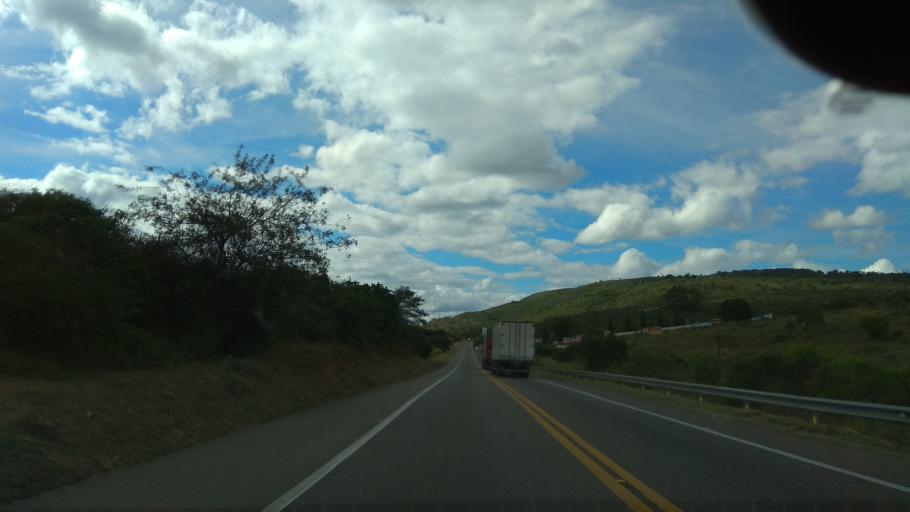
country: BR
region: Bahia
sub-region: Amargosa
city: Amargosa
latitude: -12.9108
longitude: -39.8648
